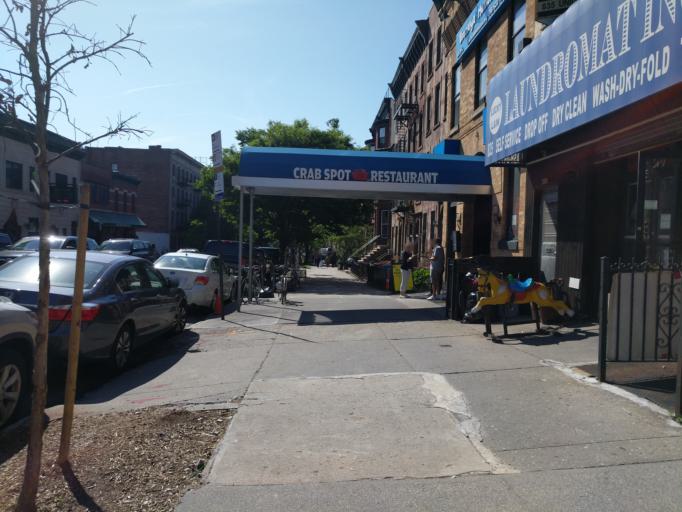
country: US
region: New York
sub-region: Kings County
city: Brooklyn
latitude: 40.6748
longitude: -73.9762
